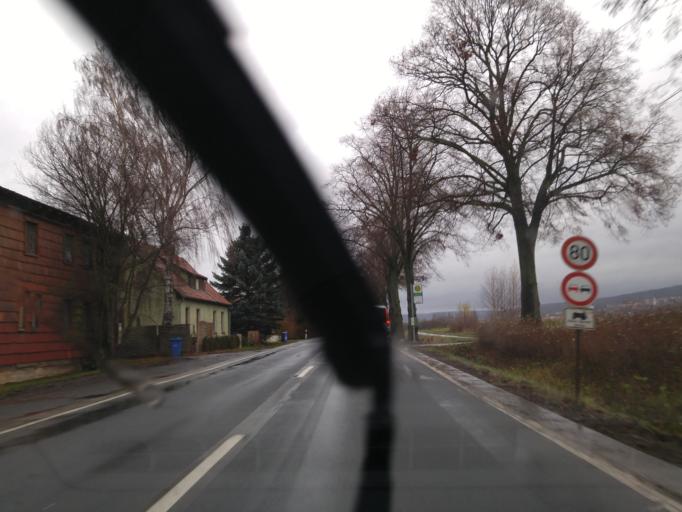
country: DE
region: Lower Saxony
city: Rosdorf
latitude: 51.4940
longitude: 9.9363
